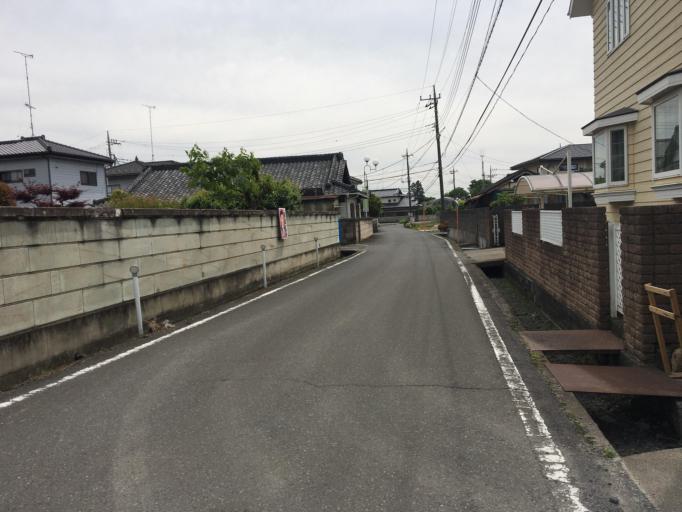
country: JP
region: Tochigi
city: Tochigi
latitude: 36.4178
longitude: 139.7499
